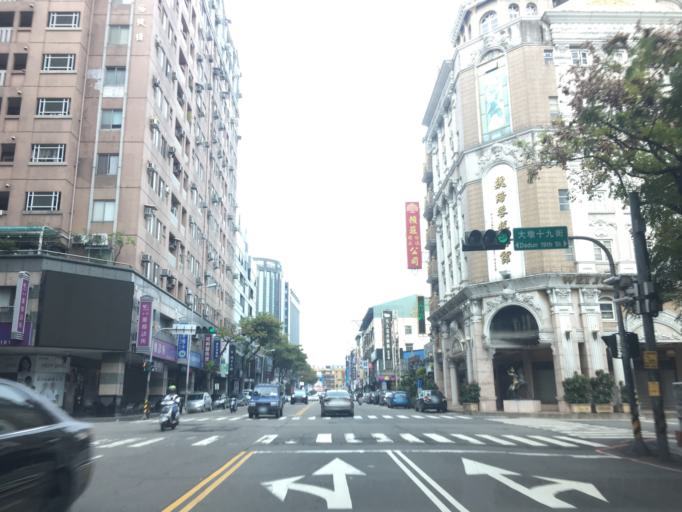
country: TW
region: Taiwan
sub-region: Taichung City
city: Taichung
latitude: 24.1566
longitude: 120.6544
